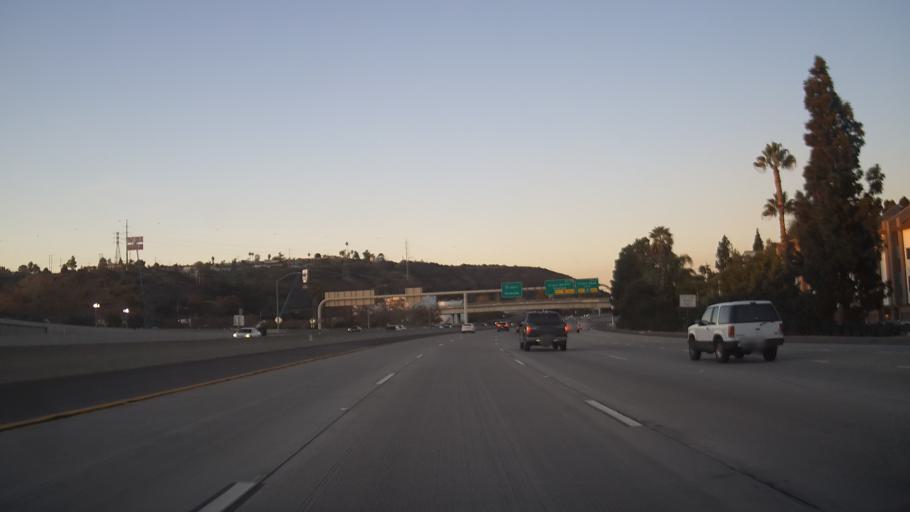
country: US
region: California
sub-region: San Diego County
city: San Diego
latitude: 32.7825
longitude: -117.1150
